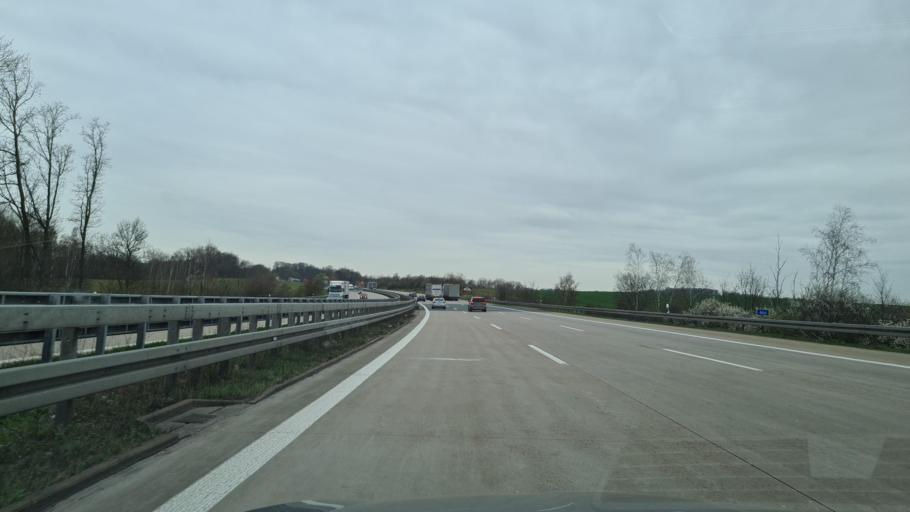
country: DE
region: Saxony
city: Hainichen
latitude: 51.0021
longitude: 13.1733
